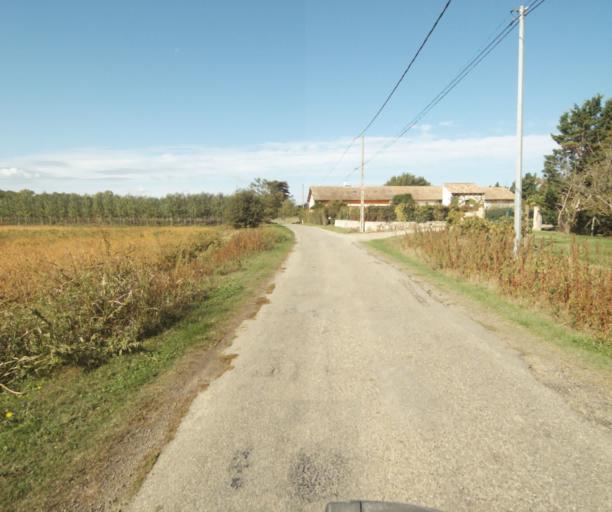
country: FR
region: Midi-Pyrenees
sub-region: Departement du Tarn-et-Garonne
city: Verdun-sur-Garonne
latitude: 43.8688
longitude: 1.2411
